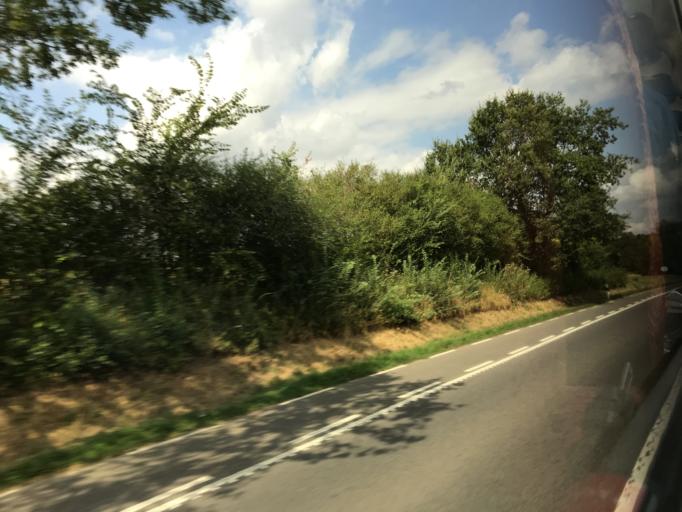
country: LU
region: Luxembourg
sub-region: Canton de Luxembourg
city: Weiler-la-Tour
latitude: 49.5368
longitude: 6.1779
